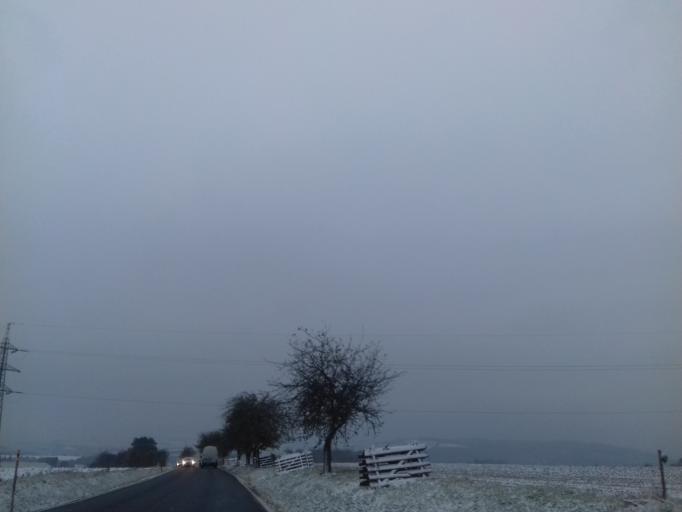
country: CZ
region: Plzensky
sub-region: Okres Domazlice
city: Domazlice
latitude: 49.4647
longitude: 12.9345
